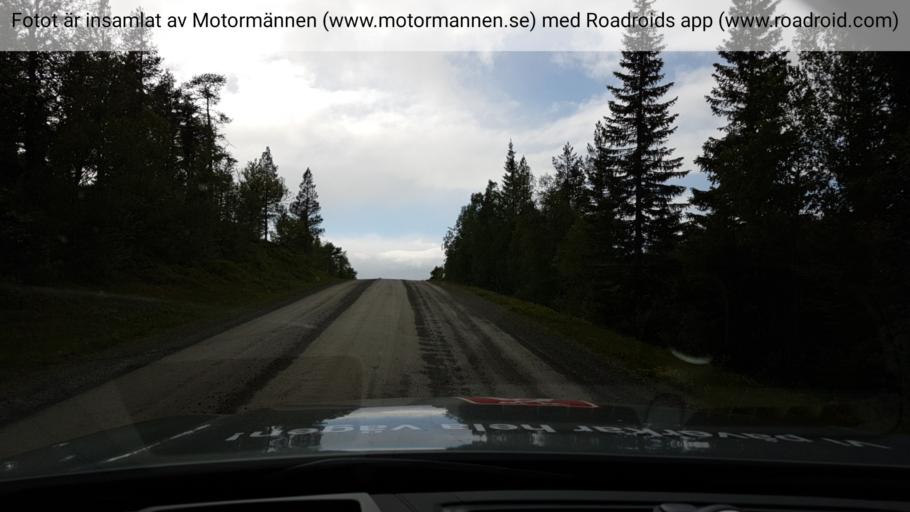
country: NO
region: Nord-Trondelag
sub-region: Snasa
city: Snaase
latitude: 63.7323
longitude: 12.5220
